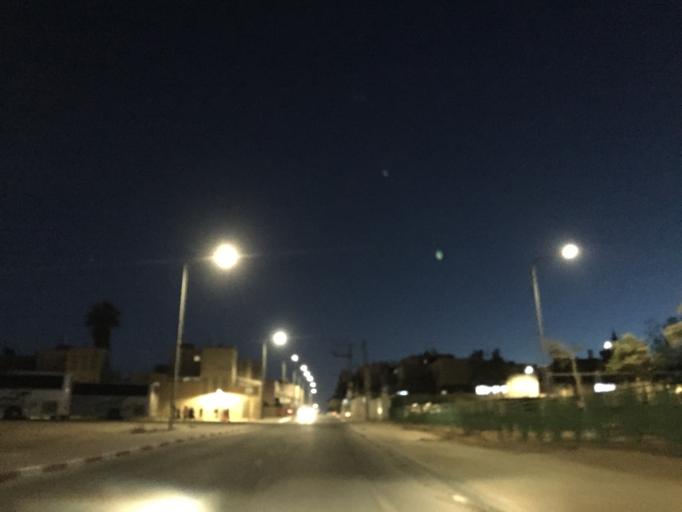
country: IL
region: Southern District
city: Mitzpe Ramon
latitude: 30.6137
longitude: 34.8006
